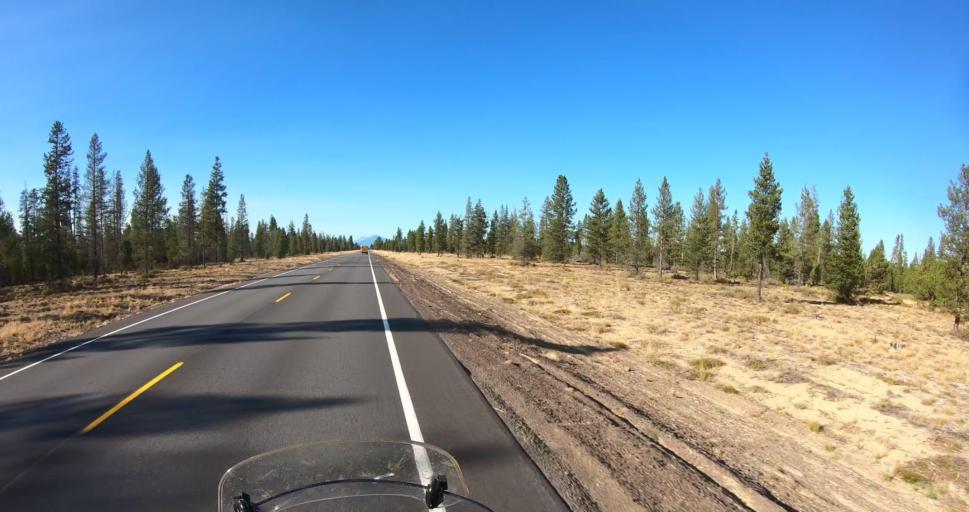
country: US
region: Oregon
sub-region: Deschutes County
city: La Pine
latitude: 43.5868
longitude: -121.4905
